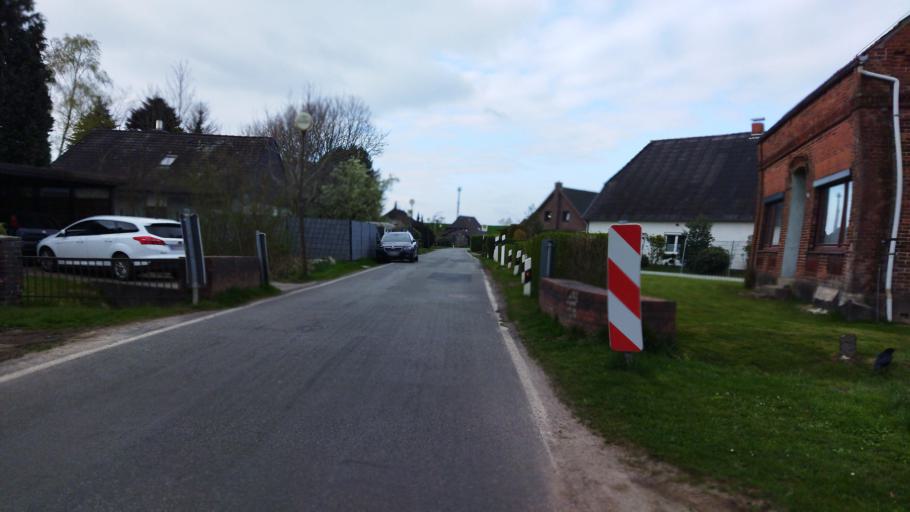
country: DE
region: Lower Saxony
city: Lemwerder
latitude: 53.1653
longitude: 8.5819
